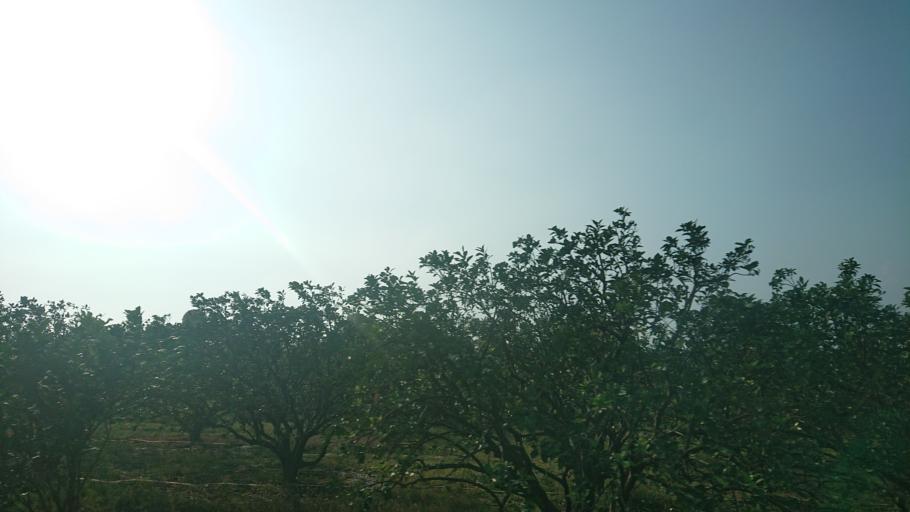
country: TW
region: Taiwan
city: Xinying
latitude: 23.1600
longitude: 120.2501
